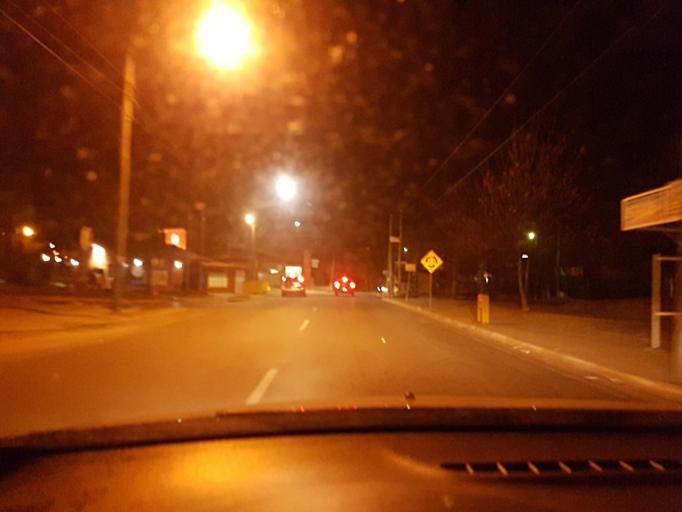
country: AR
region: Cordoba
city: Villa Allende
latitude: -31.2914
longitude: -64.2926
